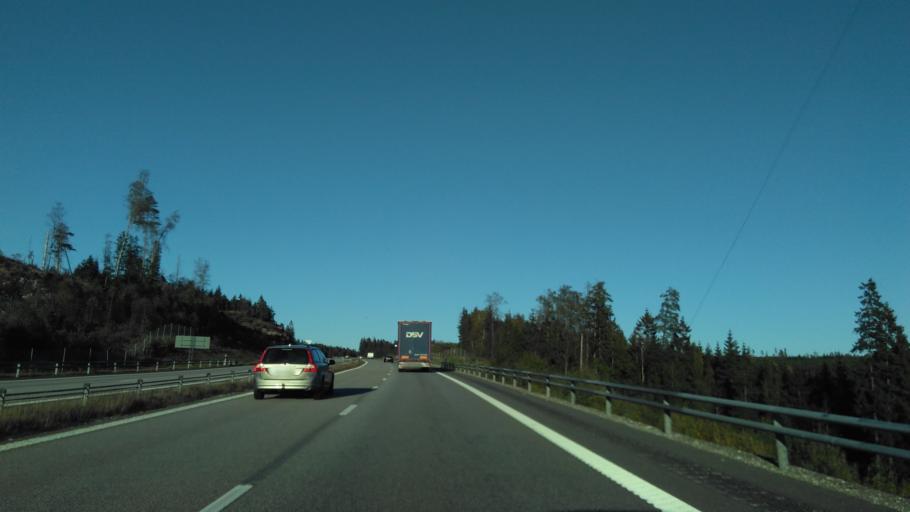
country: SE
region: Vaestra Goetaland
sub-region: Boras Kommun
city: Ganghester
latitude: 57.7316
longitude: 13.0326
